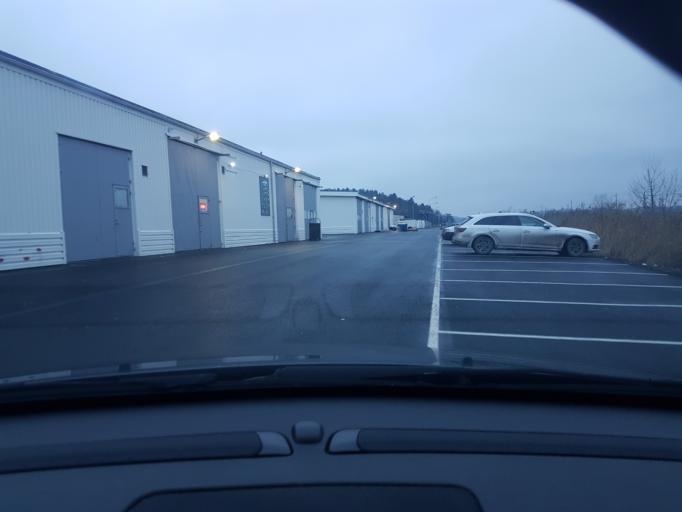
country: SE
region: Vaestra Goetaland
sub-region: Ale Kommun
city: Alvangen
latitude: 57.9519
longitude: 12.1013
